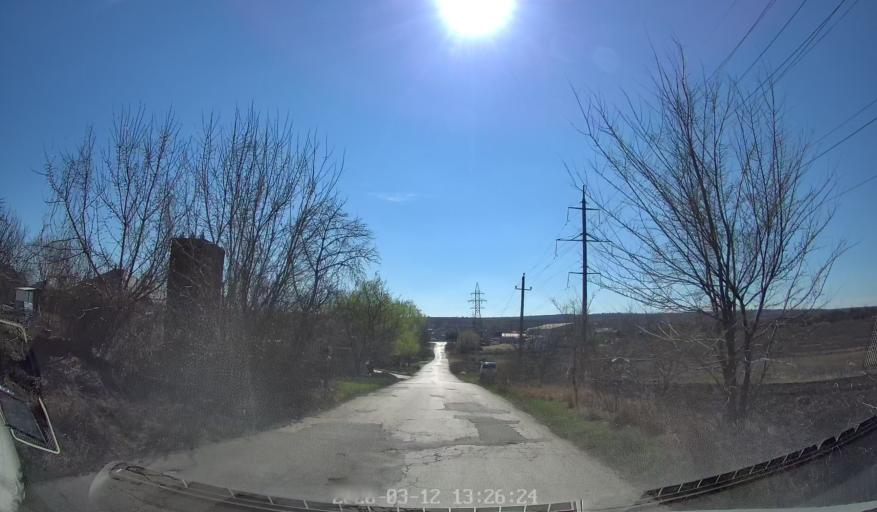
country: MD
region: Laloveni
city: Ialoveni
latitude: 46.9347
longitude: 28.8149
